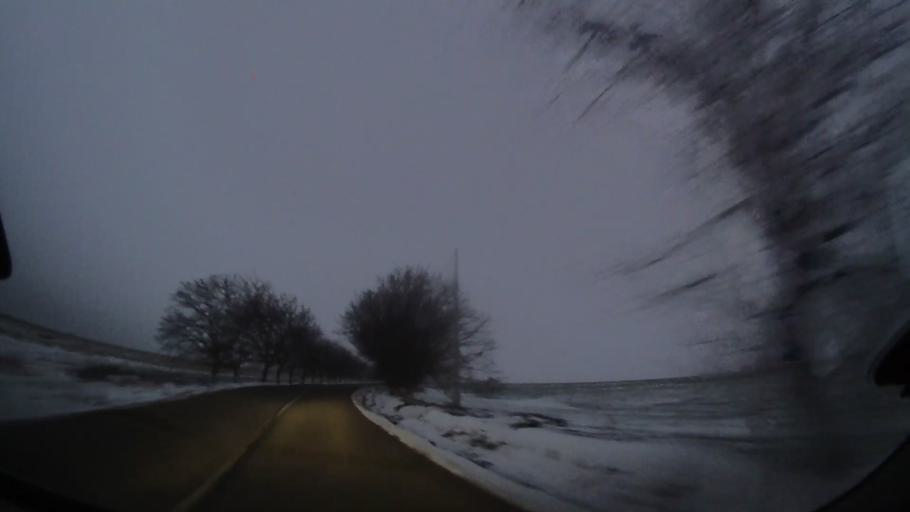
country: RO
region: Vaslui
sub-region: Comuna Dimitrie Cantemir
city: Dimitrie Cantemir
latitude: 46.5141
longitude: 28.0317
